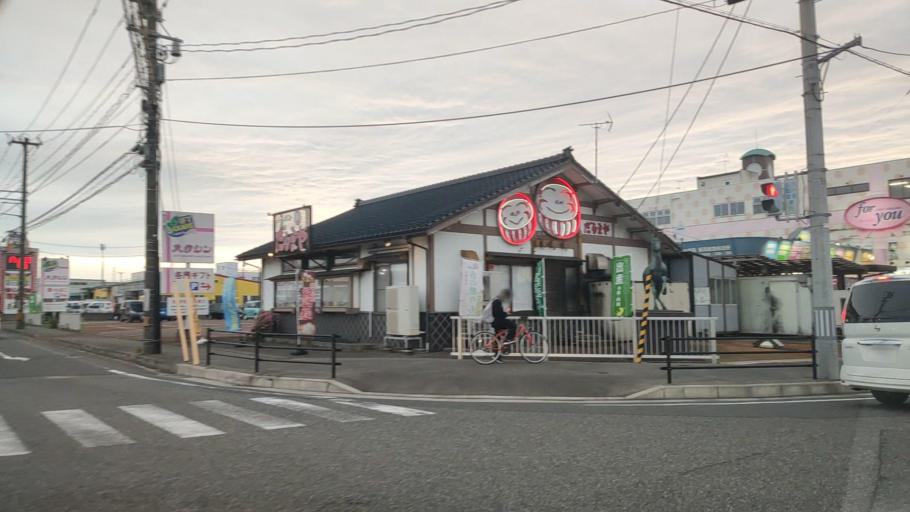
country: JP
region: Niigata
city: Kameda-honcho
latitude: 37.9108
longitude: 139.0989
